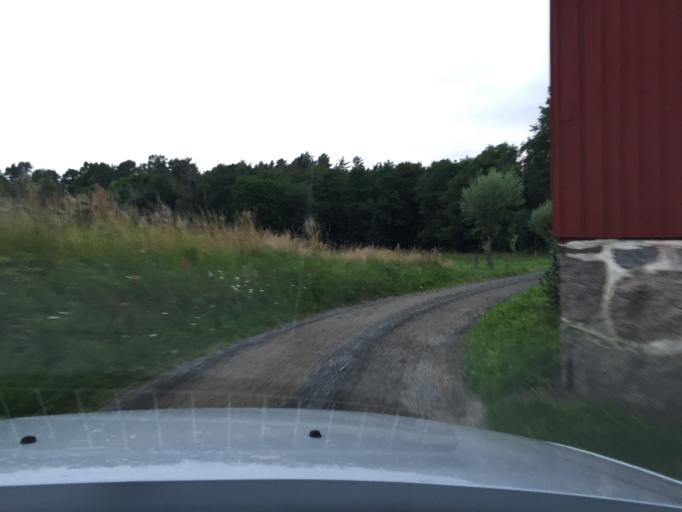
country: SE
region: Skane
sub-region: Kristianstads Kommun
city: Degeberga
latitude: 55.7271
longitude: 14.1255
